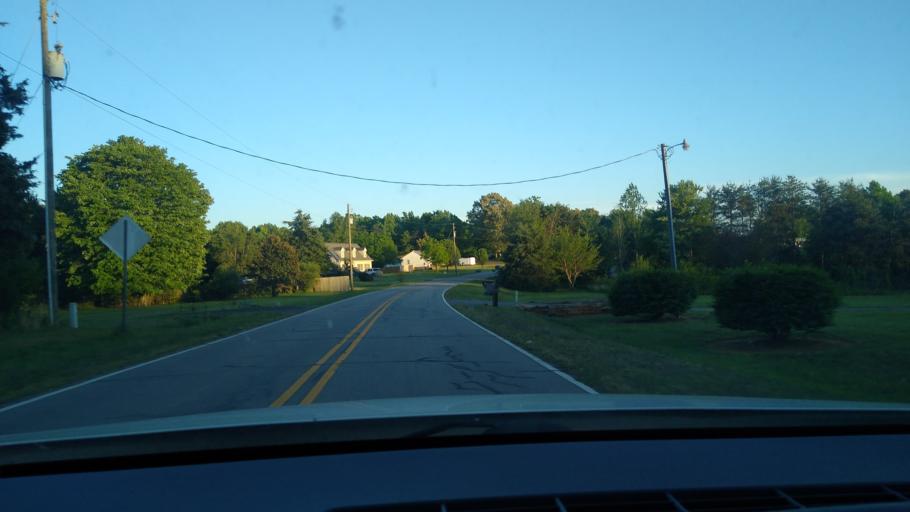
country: US
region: North Carolina
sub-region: Rockingham County
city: Reidsville
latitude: 36.3916
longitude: -79.5534
